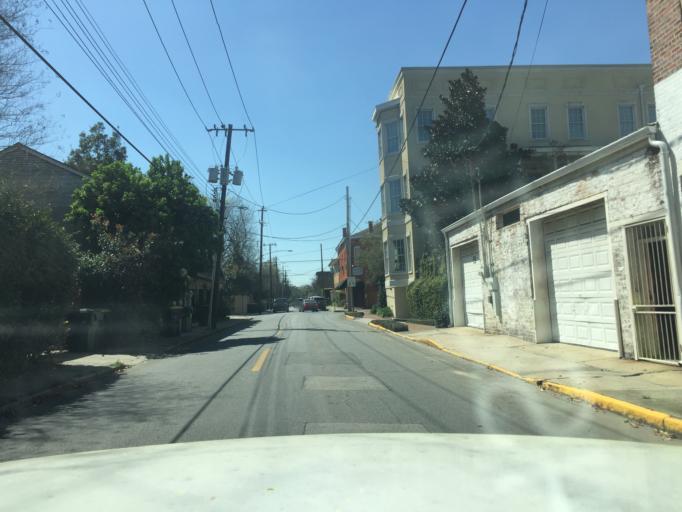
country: US
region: Georgia
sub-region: Chatham County
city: Savannah
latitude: 32.0741
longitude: -81.0975
